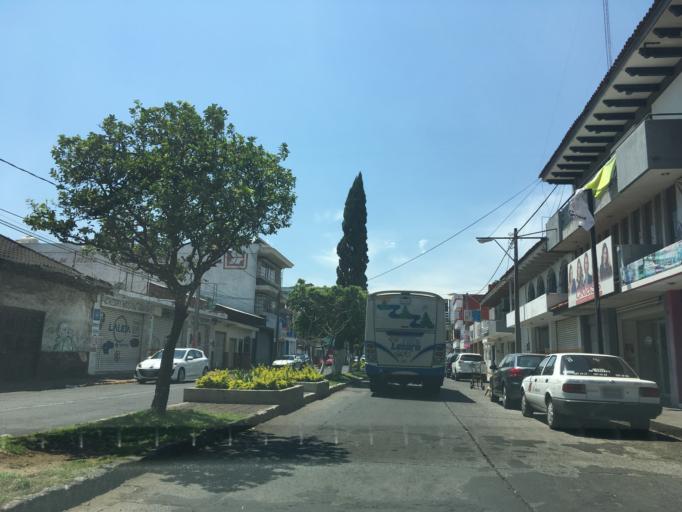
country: MX
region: Michoacan
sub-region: Uruapan
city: Uruapan
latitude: 19.4150
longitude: -102.0518
